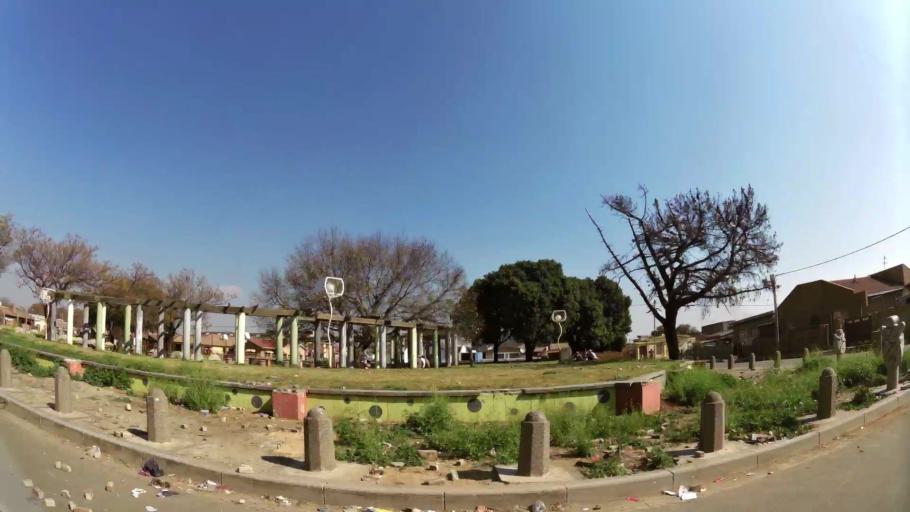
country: ZA
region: Gauteng
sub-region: Ekurhuleni Metropolitan Municipality
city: Boksburg
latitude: -26.2167
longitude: 28.2920
